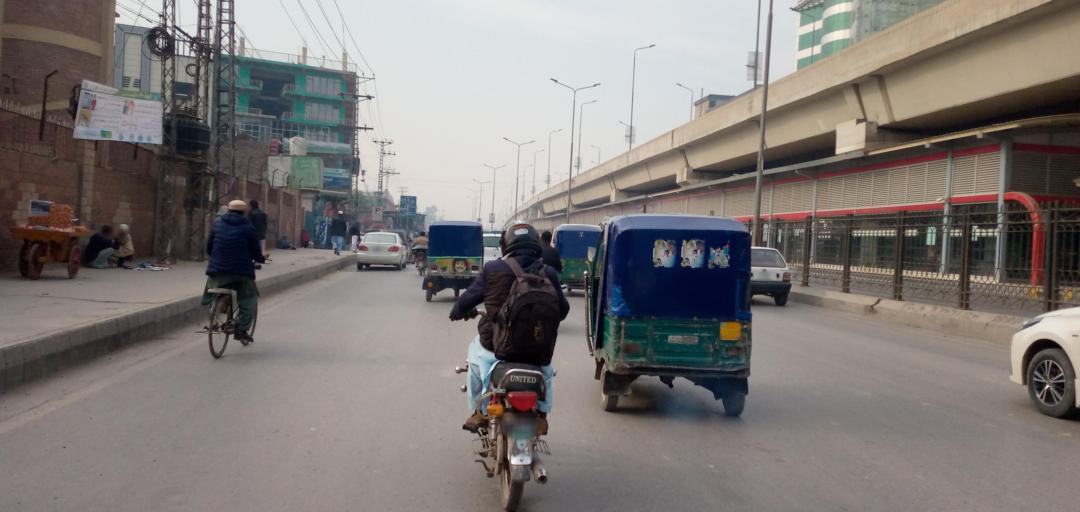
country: PK
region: Khyber Pakhtunkhwa
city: Peshawar
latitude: 34.0145
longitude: 71.5748
